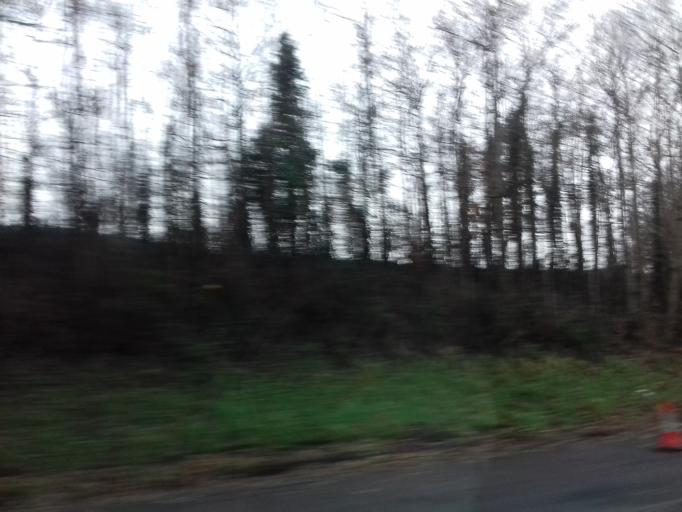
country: IE
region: Ulster
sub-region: County Donegal
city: Raphoe
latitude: 54.9412
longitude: -7.6220
